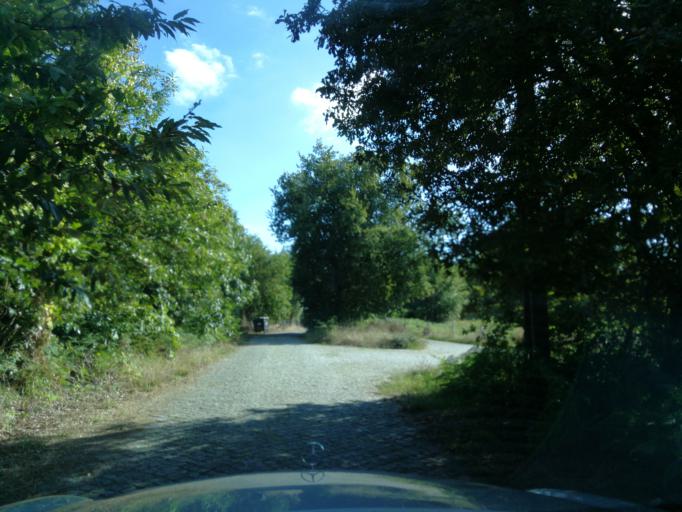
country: PT
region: Braga
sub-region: Braga
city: Adaufe
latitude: 41.5745
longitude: -8.3840
